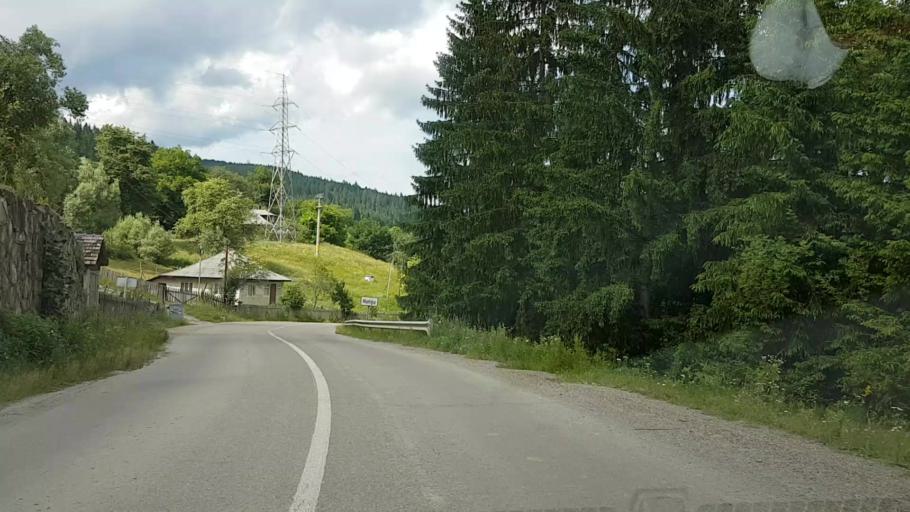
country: RO
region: Neamt
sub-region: Comuna Hangu
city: Hangu
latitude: 47.0566
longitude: 26.0309
